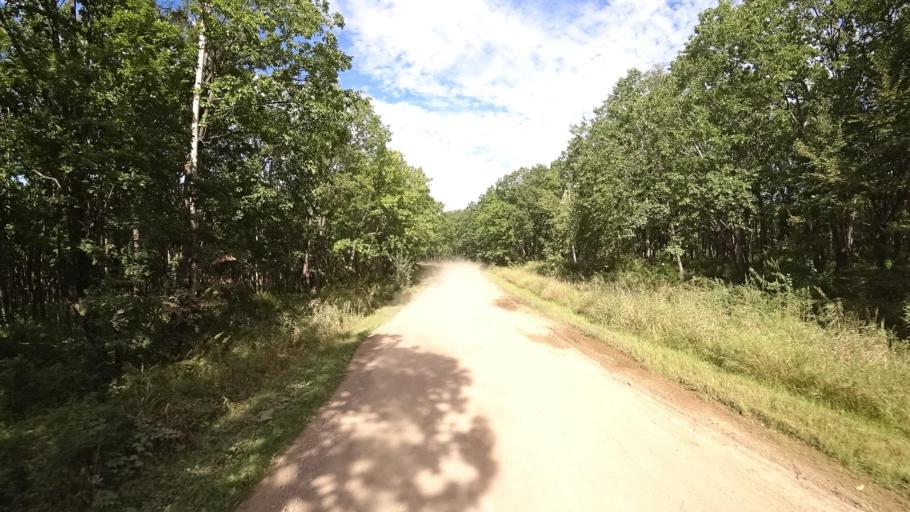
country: RU
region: Primorskiy
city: Yakovlevka
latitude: 44.4070
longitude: 133.5681
